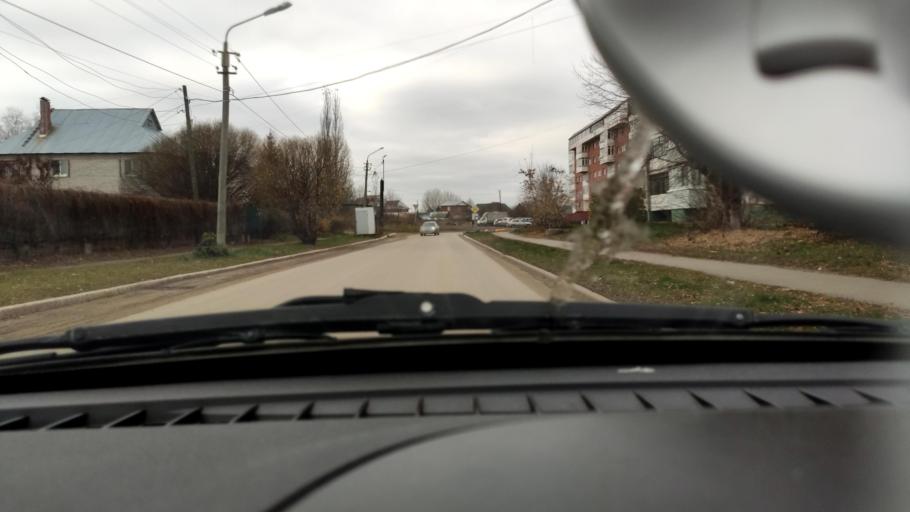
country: RU
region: Perm
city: Kondratovo
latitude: 57.9744
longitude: 56.1042
